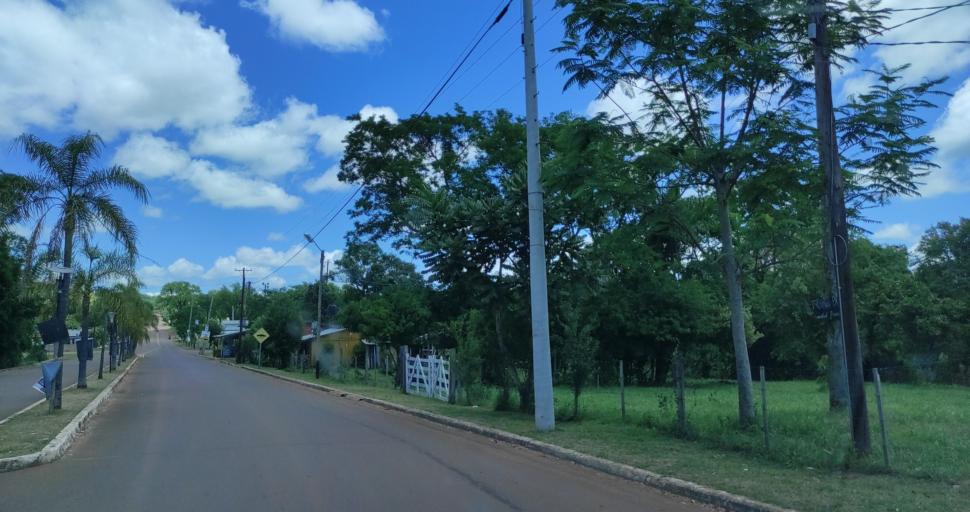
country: AR
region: Misiones
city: Cerro Cora
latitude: -27.5102
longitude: -55.6055
